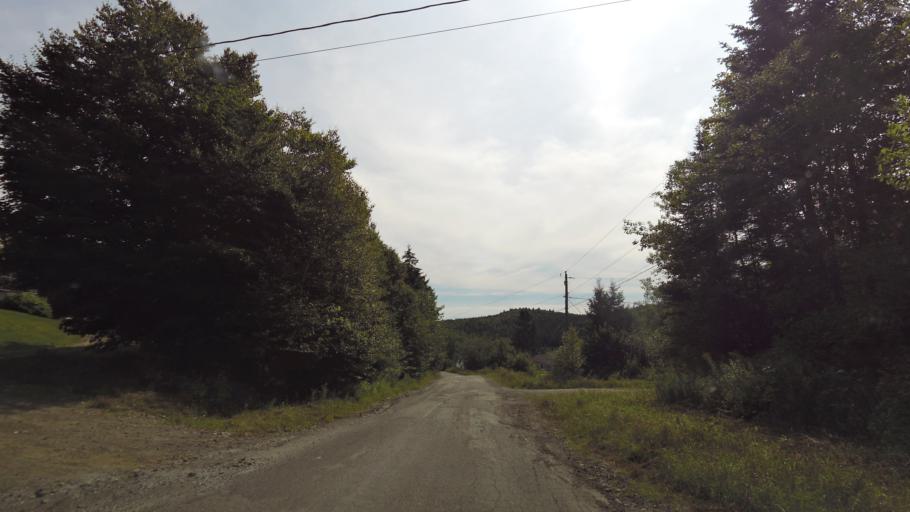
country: CA
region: New Brunswick
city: Hampton
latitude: 45.5620
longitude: -65.8442
